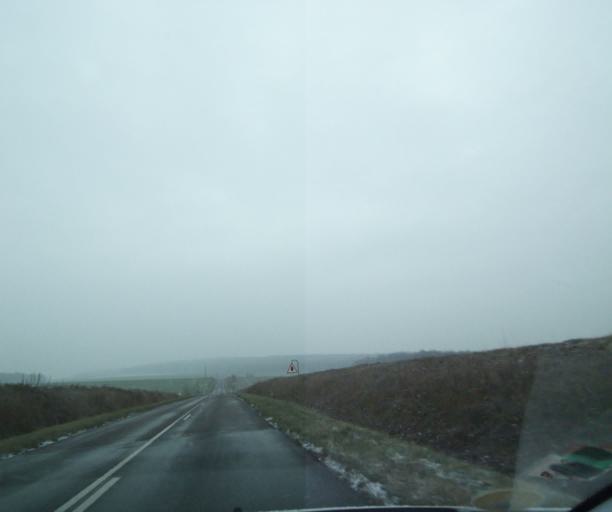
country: FR
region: Champagne-Ardenne
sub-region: Departement de la Haute-Marne
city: Wassy
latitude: 48.4817
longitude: 4.9976
